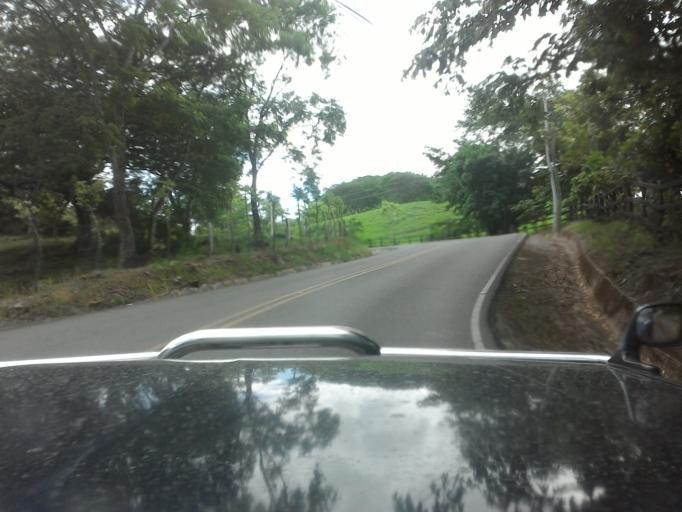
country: CR
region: Puntarenas
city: Miramar
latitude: 10.1890
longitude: -84.8398
